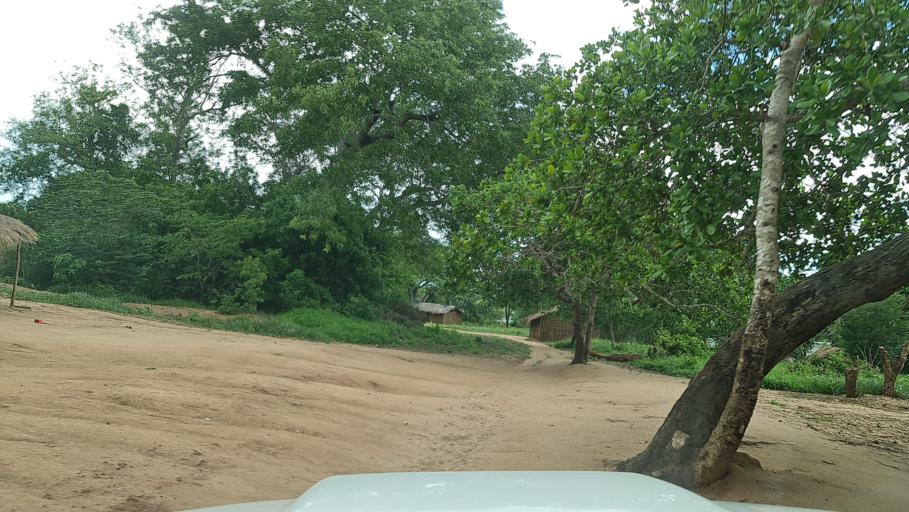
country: MZ
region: Nampula
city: Ilha de Mocambique
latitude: -15.4966
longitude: 40.1612
